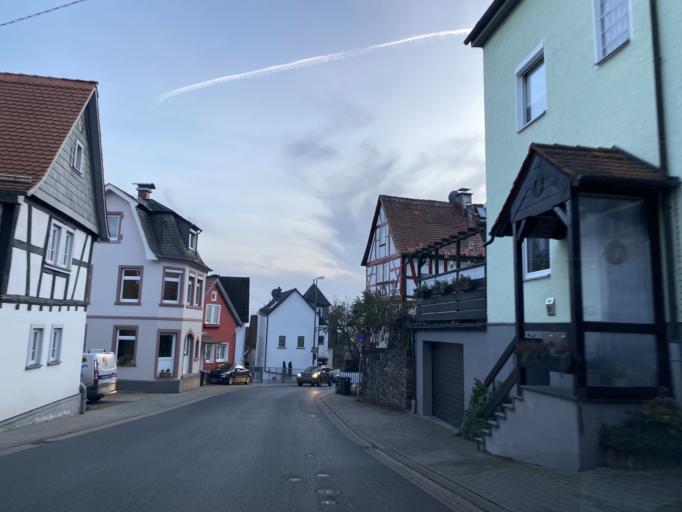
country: DE
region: Hesse
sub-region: Regierungsbezirk Darmstadt
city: Konigstein im Taunus
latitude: 50.1910
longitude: 8.4787
